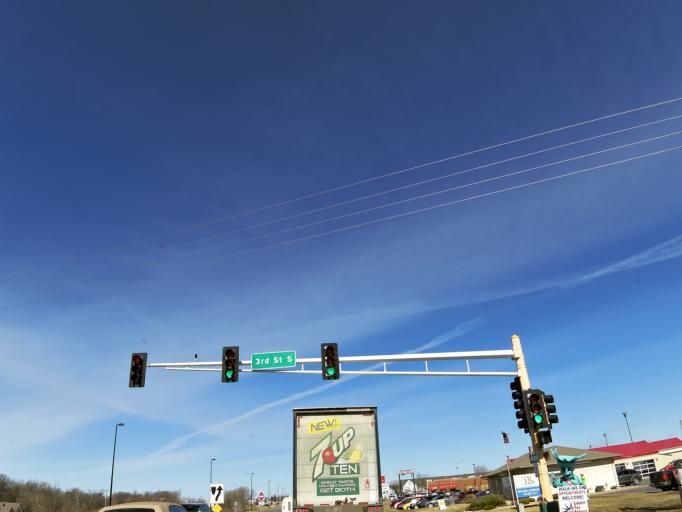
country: US
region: Minnesota
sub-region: Wright County
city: Buffalo
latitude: 45.1686
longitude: -93.8603
